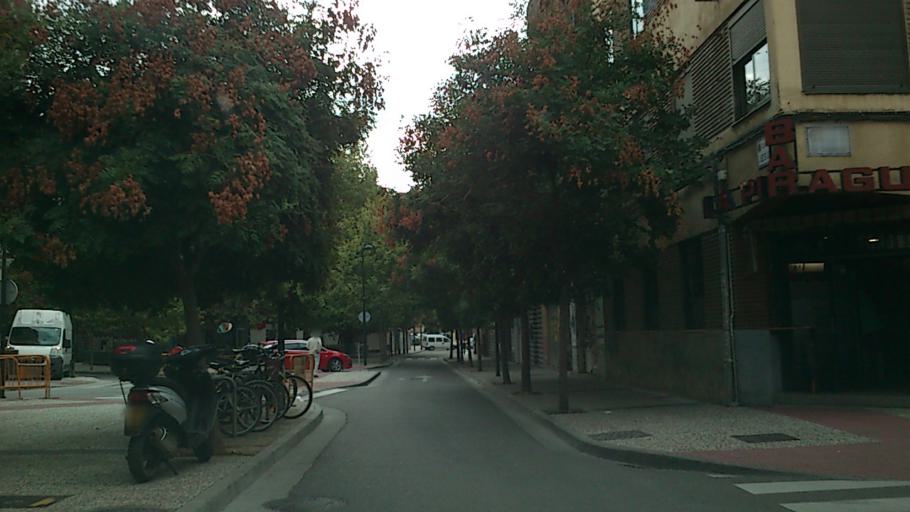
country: ES
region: Aragon
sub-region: Provincia de Zaragoza
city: Zaragoza
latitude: 41.6582
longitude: -0.8715
